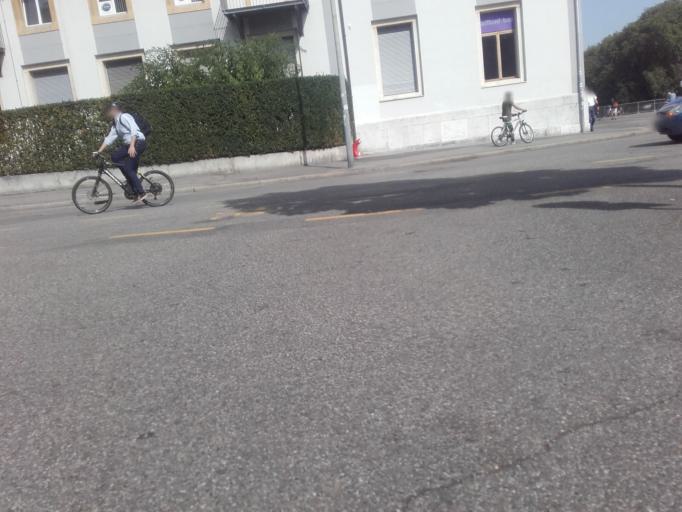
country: CH
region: Solothurn
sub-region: Bezirk Solothurn
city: Solothurn
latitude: 47.2060
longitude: 7.5348
